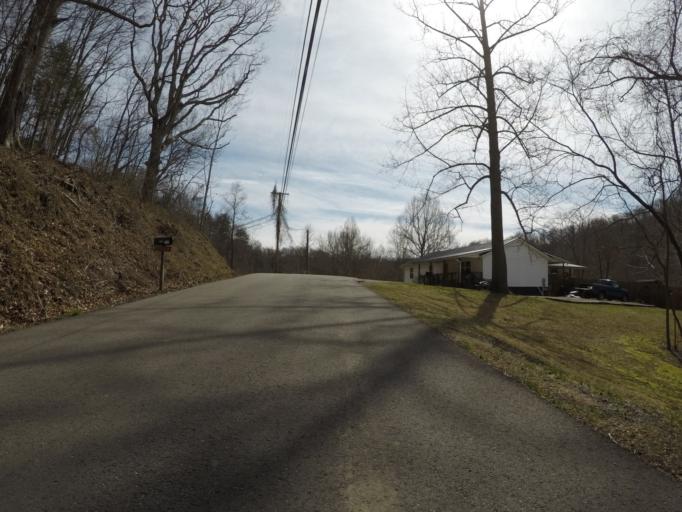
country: US
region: West Virginia
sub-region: Wayne County
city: Ceredo
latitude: 38.3763
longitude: -82.5523
